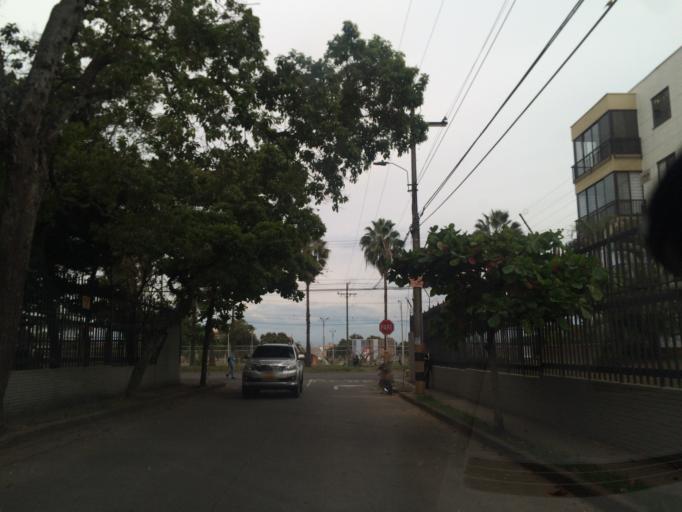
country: CO
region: Valle del Cauca
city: Cali
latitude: 3.3787
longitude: -76.5380
